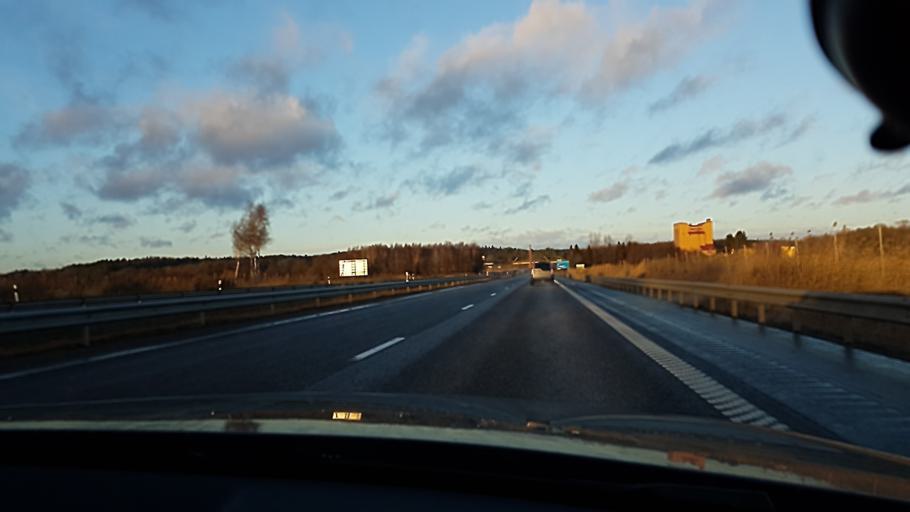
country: SE
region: Stockholm
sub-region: Sodertalje Kommun
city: Pershagen
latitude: 59.0779
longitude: 17.5942
